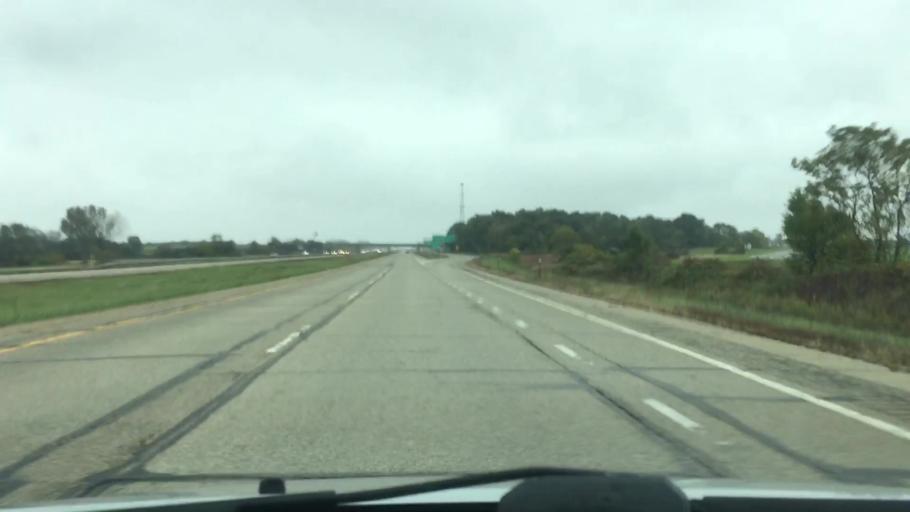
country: US
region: Wisconsin
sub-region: Walworth County
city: Elkhorn
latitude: 42.6805
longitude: -88.5263
